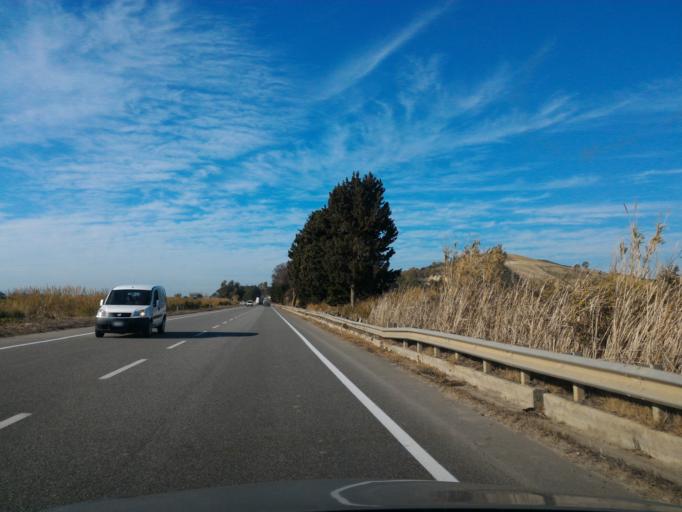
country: IT
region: Calabria
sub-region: Provincia di Catanzaro
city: Botricello
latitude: 38.9424
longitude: 16.8929
